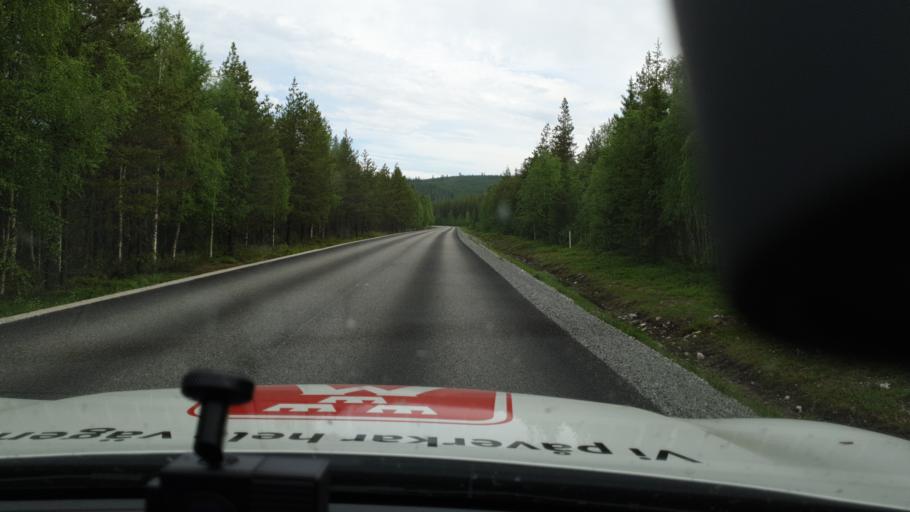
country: SE
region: Vaesterbotten
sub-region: Mala Kommun
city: Mala
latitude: 64.9336
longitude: 18.6213
